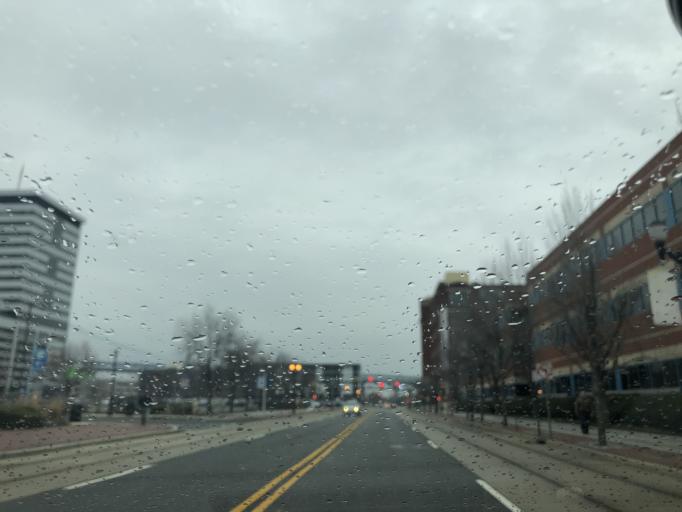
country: US
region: New Jersey
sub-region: Camden County
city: Camden
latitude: 39.9459
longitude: -75.1287
